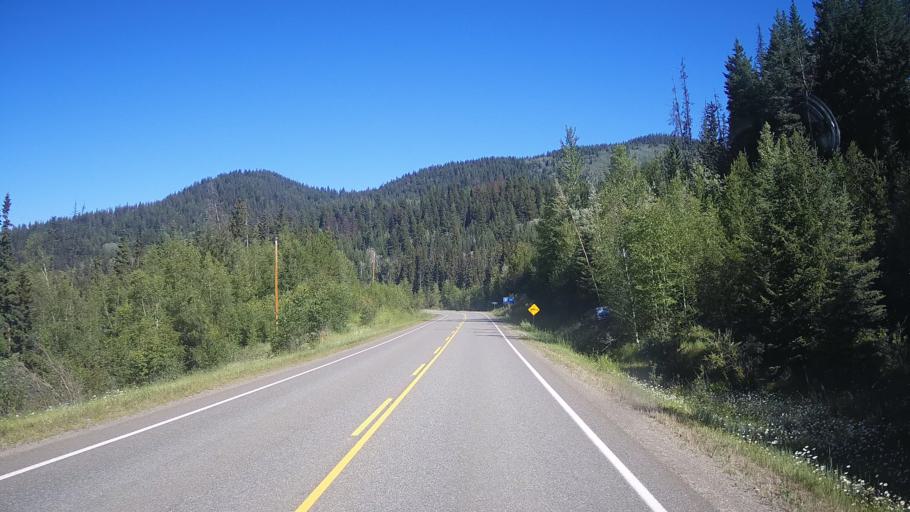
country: CA
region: British Columbia
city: Kamloops
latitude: 51.4671
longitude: -120.5321
